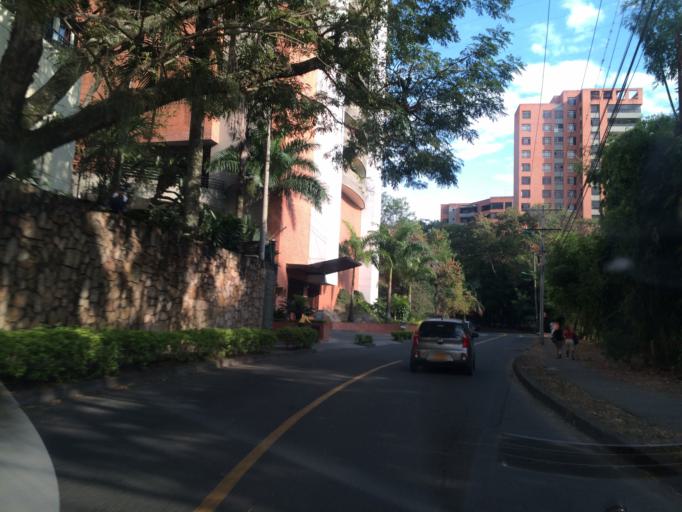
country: CO
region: Valle del Cauca
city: Cali
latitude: 3.4548
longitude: -76.5488
